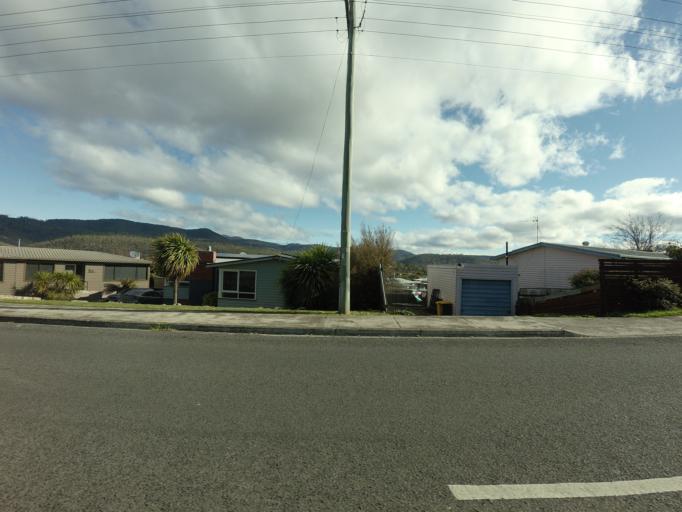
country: AU
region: Tasmania
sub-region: Derwent Valley
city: New Norfolk
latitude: -42.7712
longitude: 147.0475
